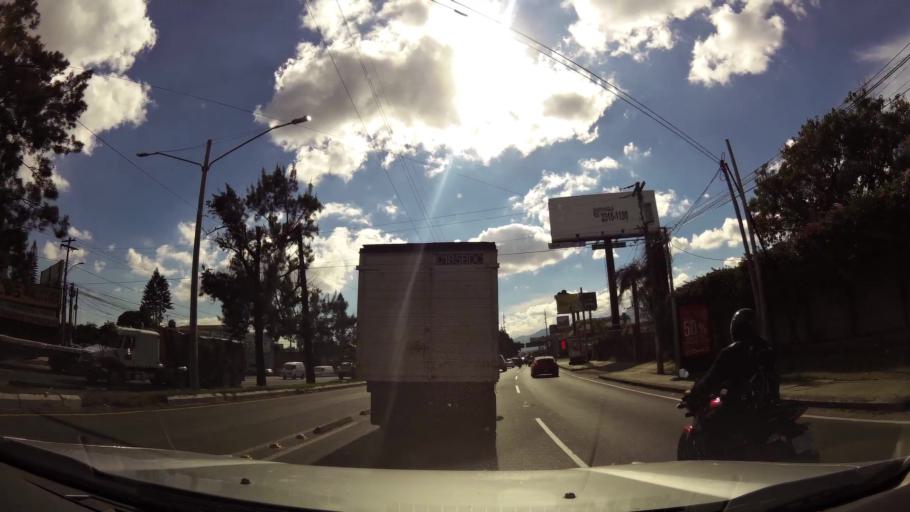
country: GT
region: Guatemala
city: Villa Nueva
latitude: 14.5776
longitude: -90.5696
